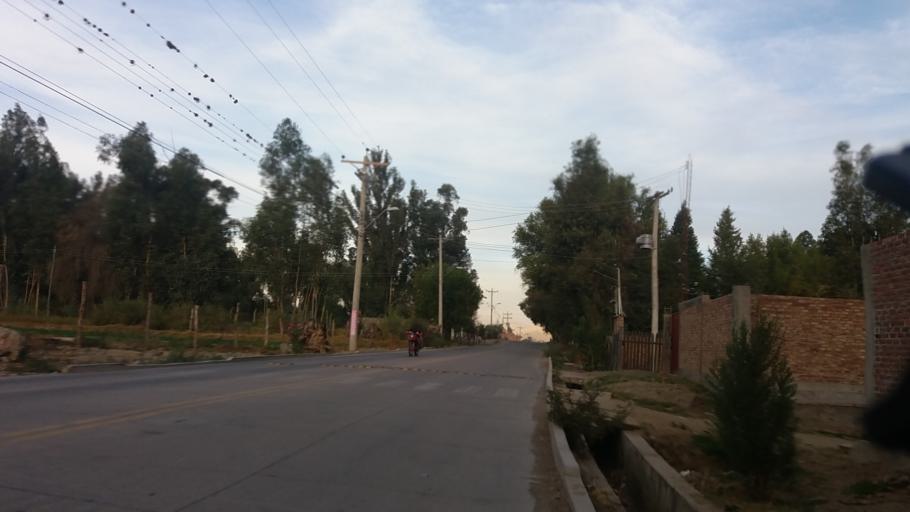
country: BO
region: Cochabamba
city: Cochabamba
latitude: -17.3639
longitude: -66.2209
